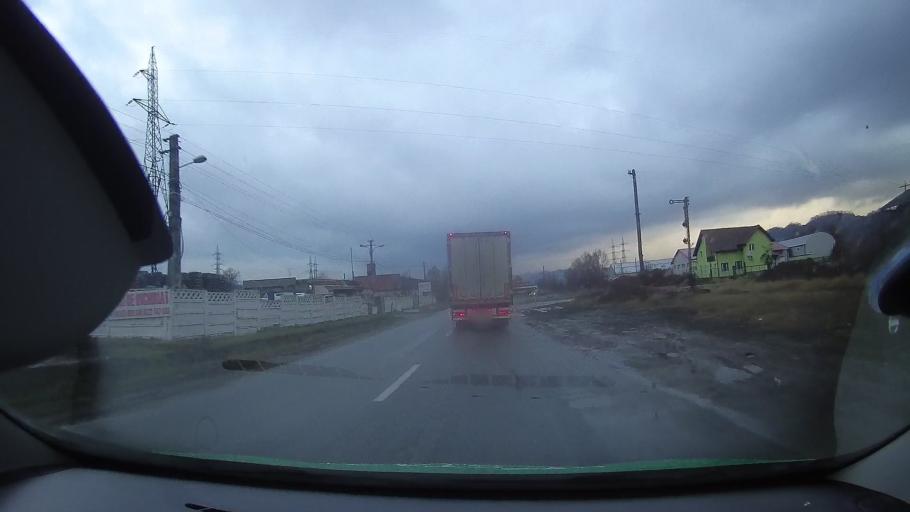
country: RO
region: Hunedoara
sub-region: Municipiul Brad
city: Brad
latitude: 46.1419
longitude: 22.7762
